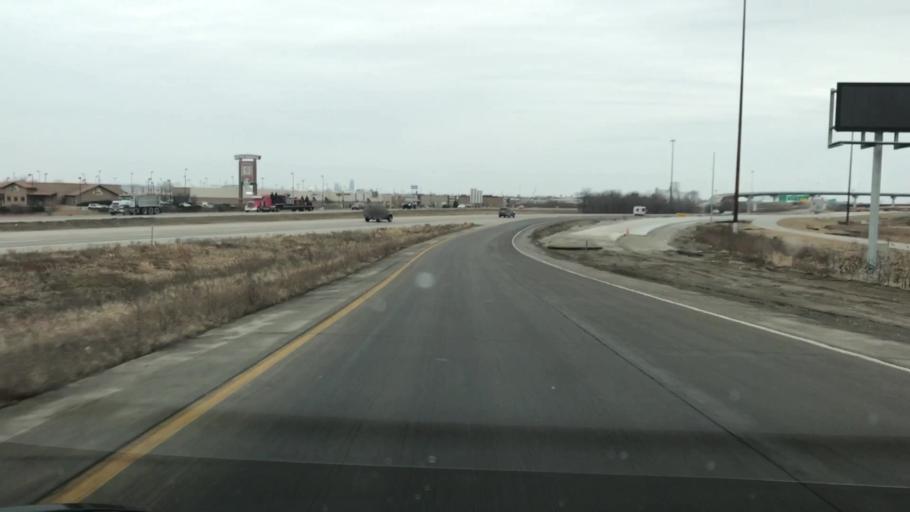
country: US
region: Iowa
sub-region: Pottawattamie County
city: Council Bluffs
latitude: 41.2221
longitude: -95.8328
